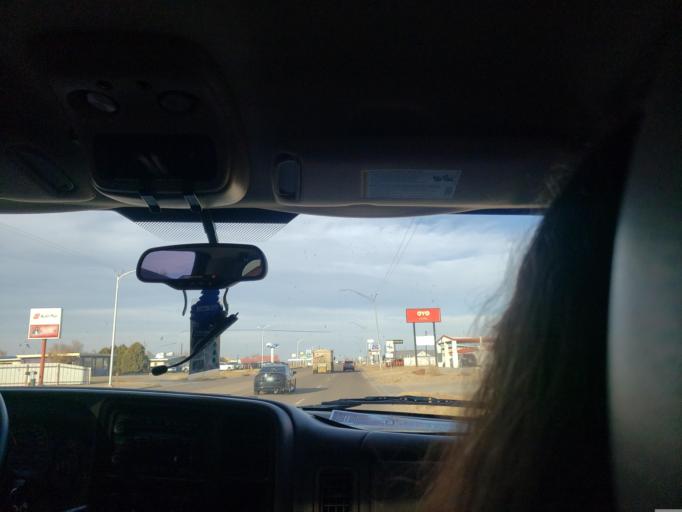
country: US
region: Oklahoma
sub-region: Texas County
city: Guymon
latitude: 36.6863
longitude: -101.4688
